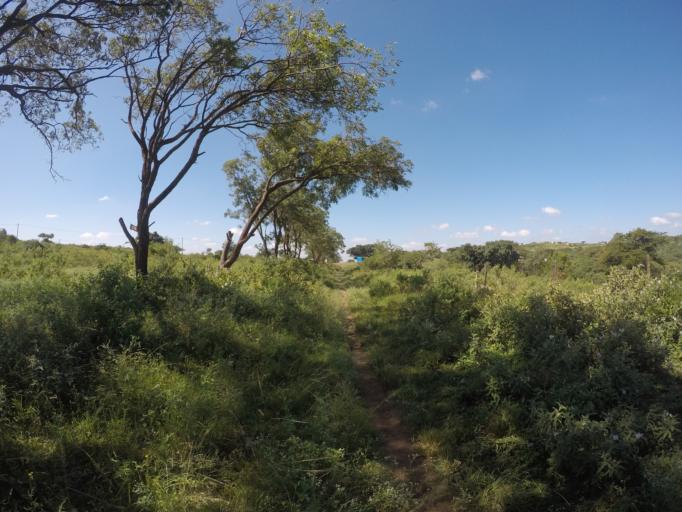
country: ZA
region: KwaZulu-Natal
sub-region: uThungulu District Municipality
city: Empangeni
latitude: -28.5633
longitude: 31.7025
